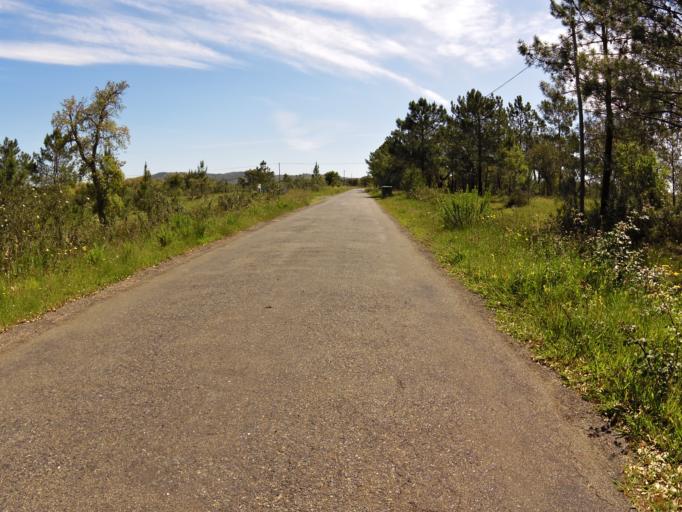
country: PT
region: Setubal
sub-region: Santiago do Cacem
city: Santiago do Cacem
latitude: 37.9393
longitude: -8.7461
